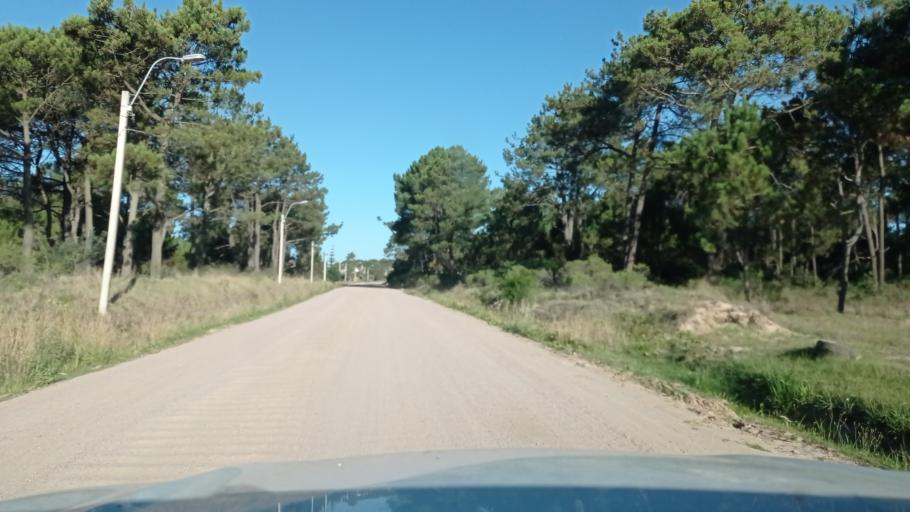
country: UY
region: Canelones
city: Pando
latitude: -34.7936
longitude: -55.9166
